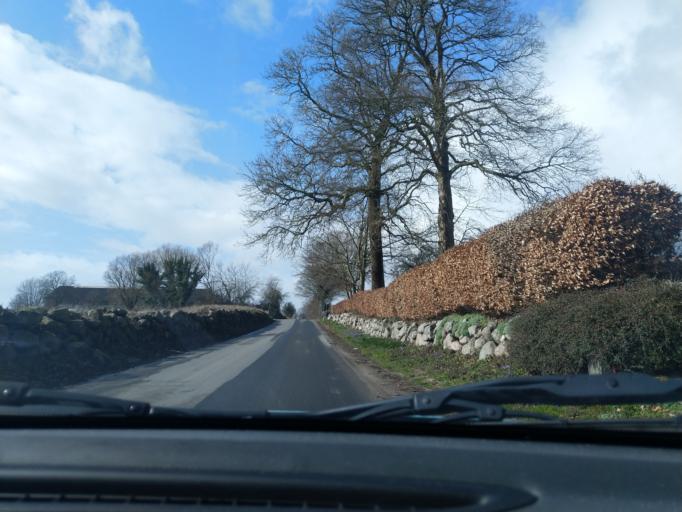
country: DK
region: Zealand
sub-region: Naestved Kommune
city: Fuglebjerg
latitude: 55.3139
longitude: 11.6698
